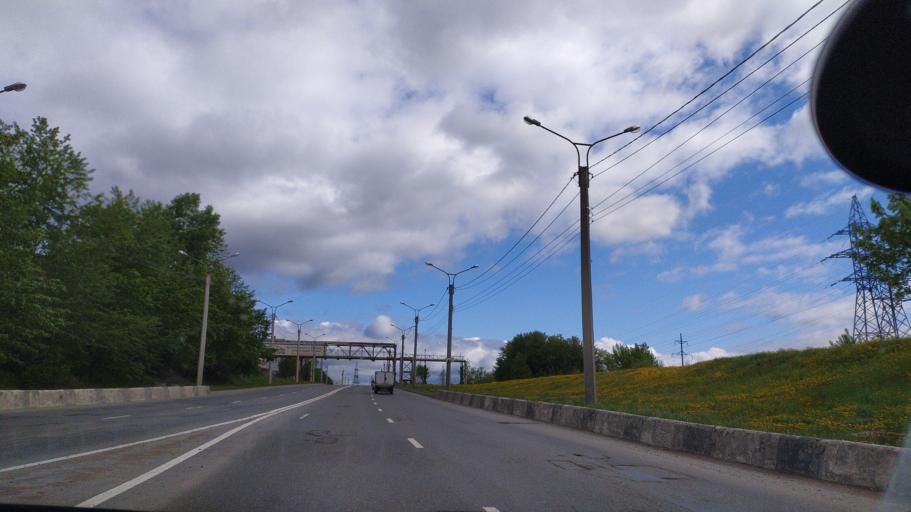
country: RU
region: Chuvashia
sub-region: Cheboksarskiy Rayon
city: Cheboksary
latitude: 56.1133
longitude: 47.2975
